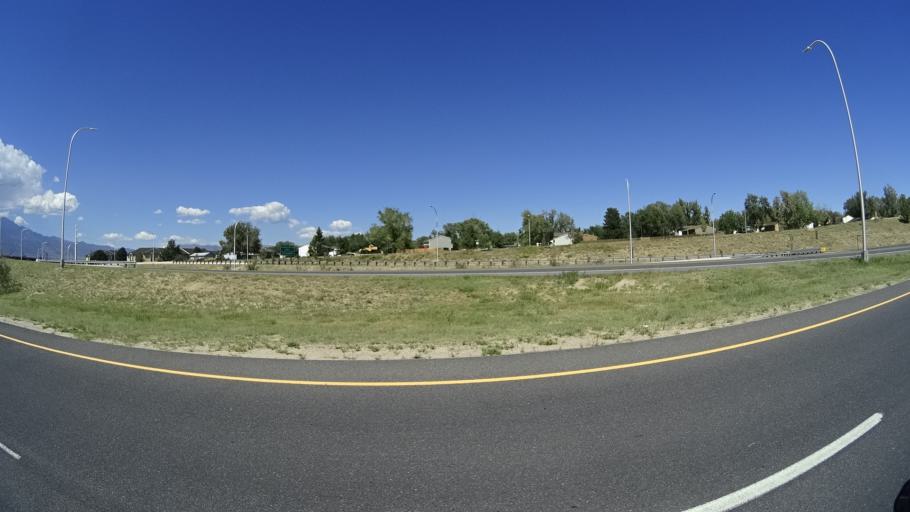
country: US
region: Colorado
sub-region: El Paso County
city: Stratmoor
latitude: 38.7807
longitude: -104.7543
